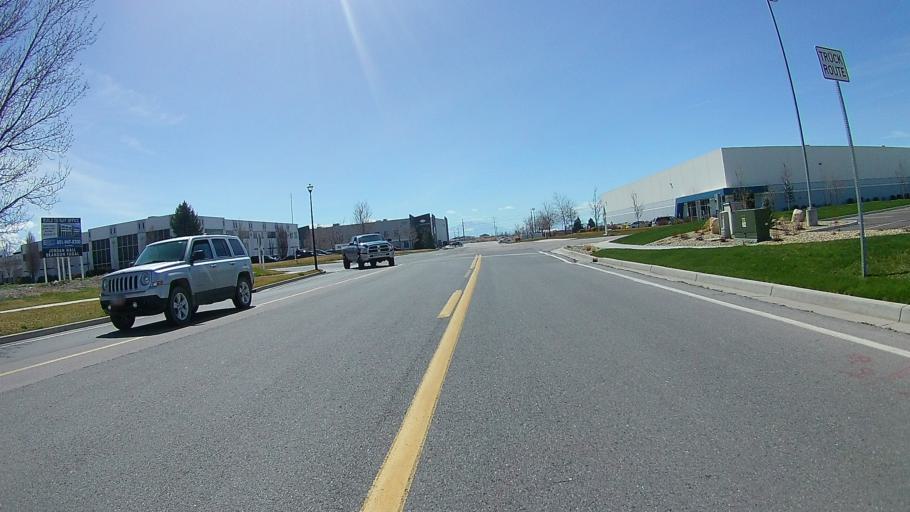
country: US
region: Utah
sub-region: Utah County
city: American Fork
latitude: 40.3520
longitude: -111.7811
